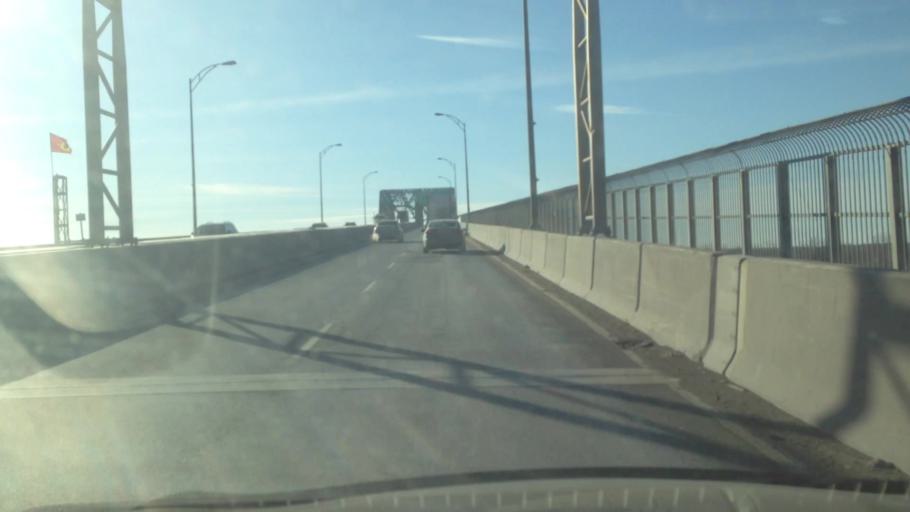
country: CA
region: Quebec
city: Montreal-Ouest
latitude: 45.4123
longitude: -73.6575
